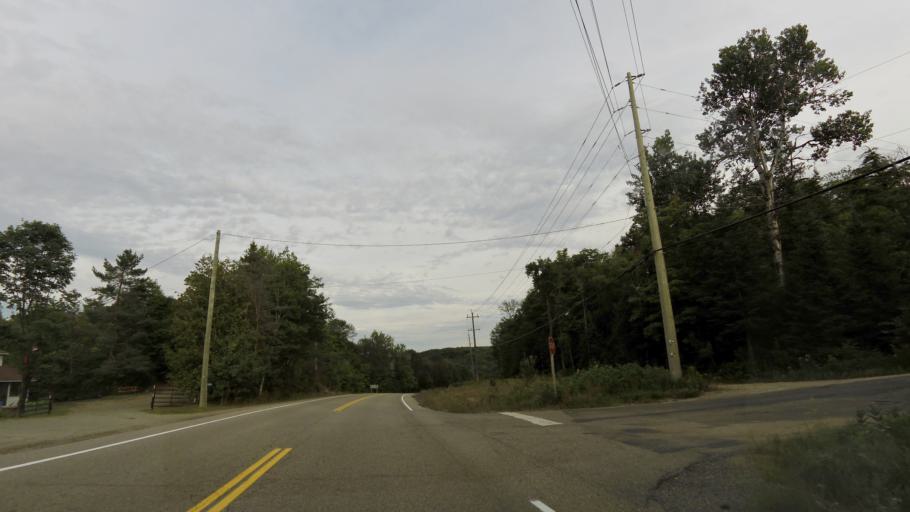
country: CA
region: Ontario
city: Bancroft
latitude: 45.0379
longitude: -78.4608
